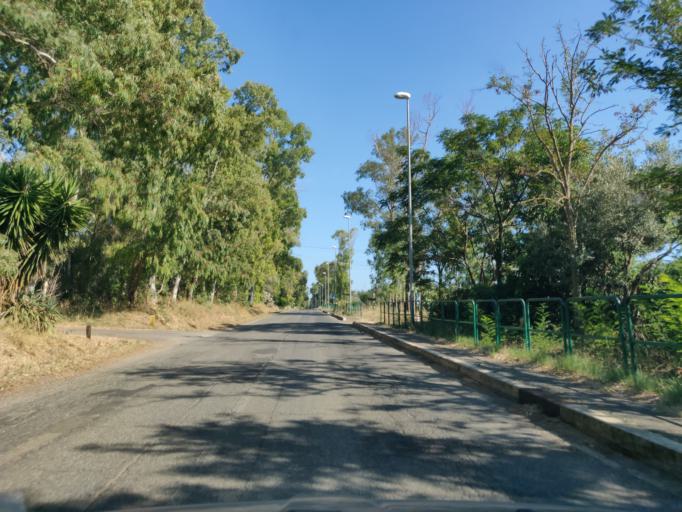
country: IT
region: Latium
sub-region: Citta metropolitana di Roma Capitale
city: Aurelia
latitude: 42.1411
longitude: 11.7657
